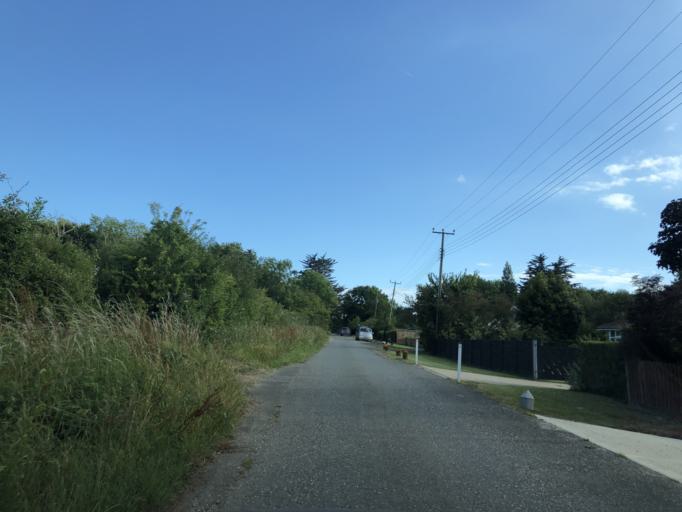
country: GB
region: England
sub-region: Isle of Wight
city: Shalfleet
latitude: 50.7056
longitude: -1.4496
